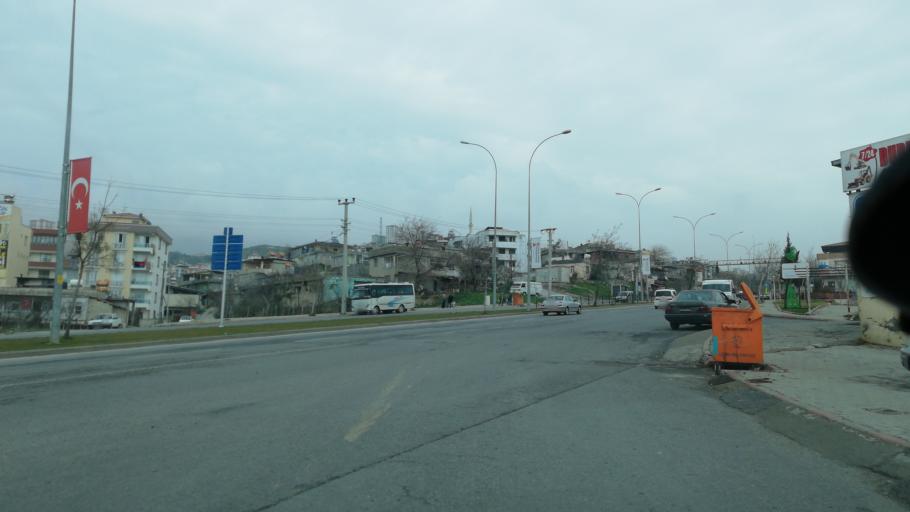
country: TR
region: Kahramanmaras
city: Kahramanmaras
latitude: 37.5679
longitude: 36.8875
